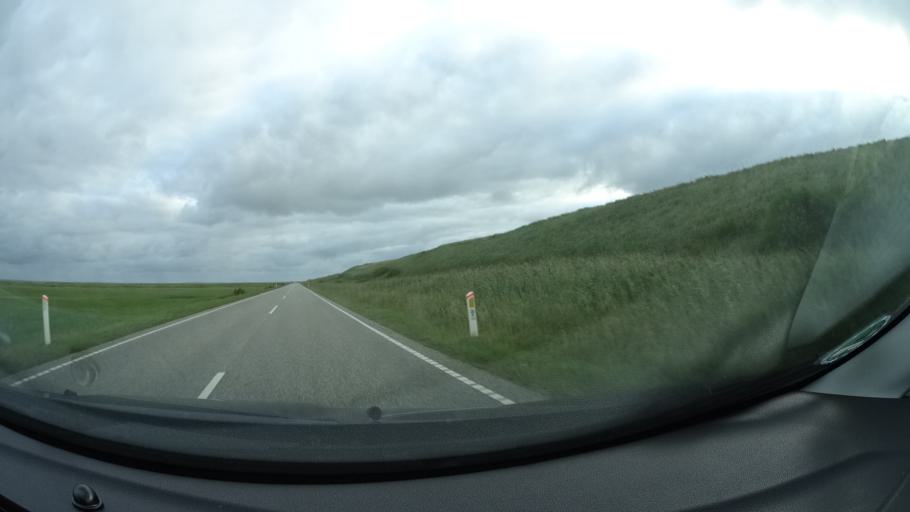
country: DK
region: Central Jutland
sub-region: Lemvig Kommune
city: Harboore
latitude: 56.4121
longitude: 8.1227
